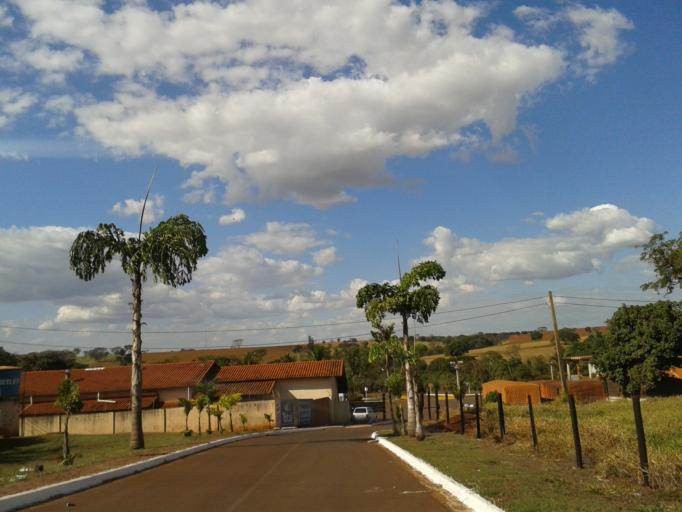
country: BR
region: Minas Gerais
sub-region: Capinopolis
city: Capinopolis
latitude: -18.6946
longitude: -49.5635
